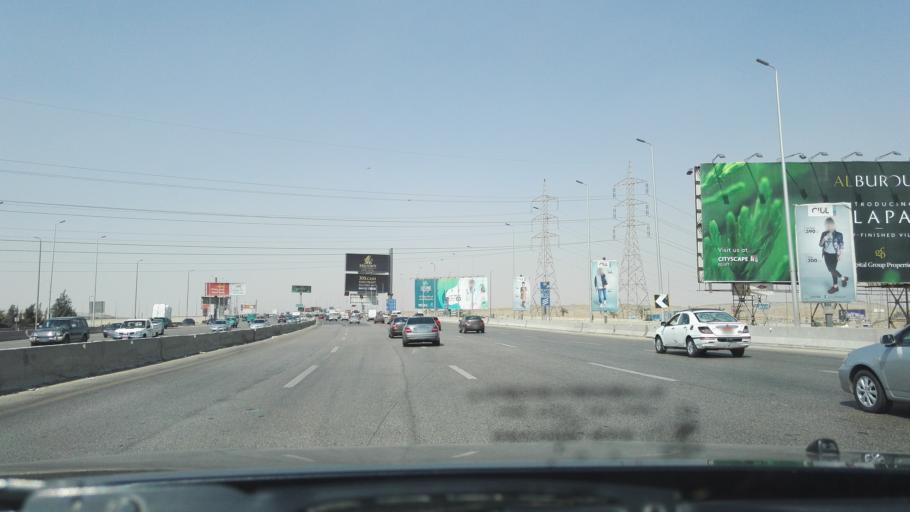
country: EG
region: Muhafazat al Qalyubiyah
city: Al Khankah
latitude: 30.0767
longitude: 31.4340
